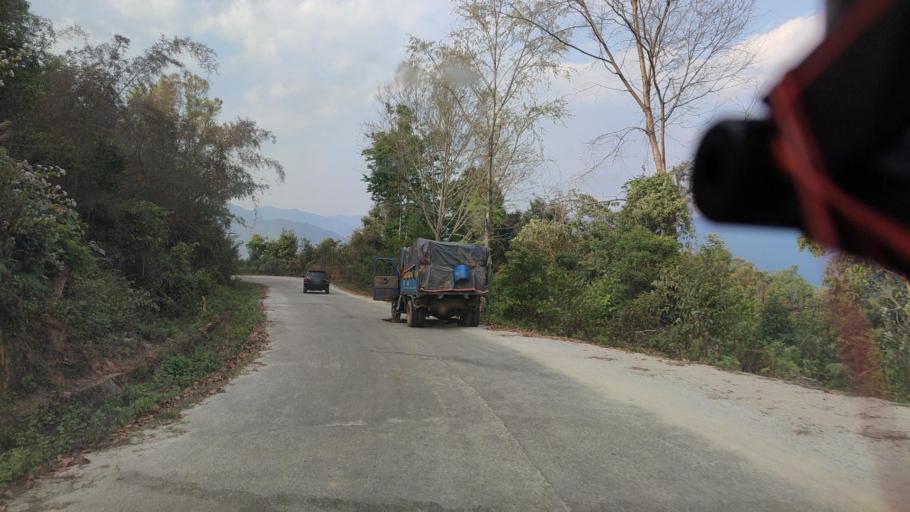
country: CN
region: Yunnan
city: Menghai
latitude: 21.4512
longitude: 99.6706
